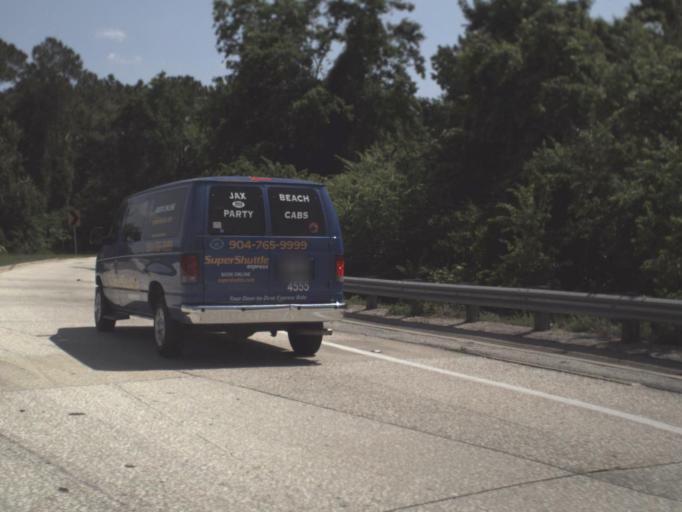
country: US
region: Florida
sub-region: Duval County
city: Jacksonville
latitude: 30.4821
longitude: -81.6434
